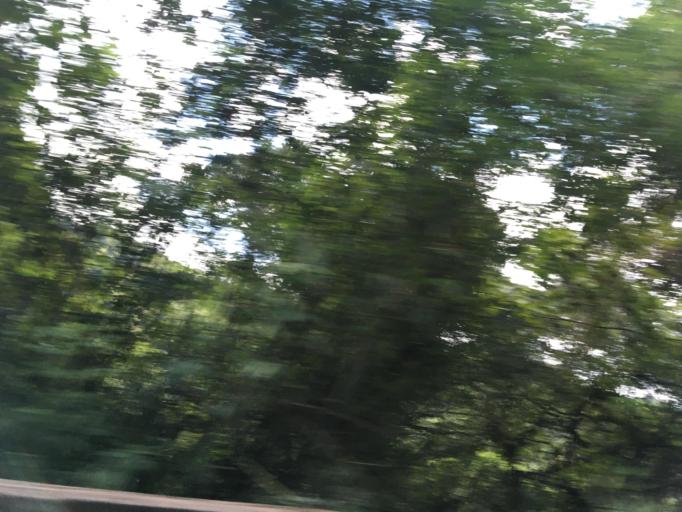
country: TW
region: Taipei
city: Taipei
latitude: 24.9493
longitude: 121.5572
